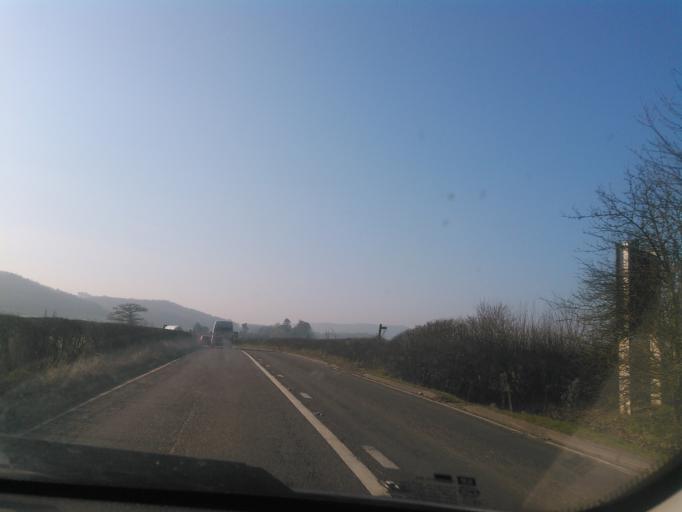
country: GB
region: England
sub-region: Shropshire
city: Craven Arms
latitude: 52.4728
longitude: -2.8206
